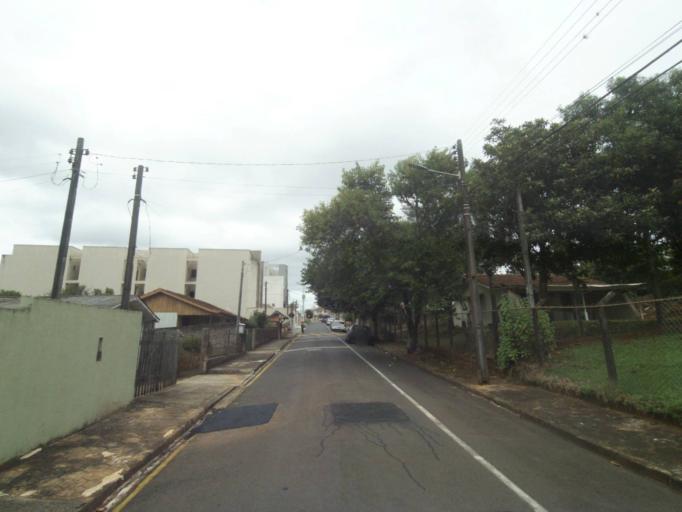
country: BR
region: Parana
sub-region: Telemaco Borba
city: Telemaco Borba
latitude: -24.3309
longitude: -50.6144
